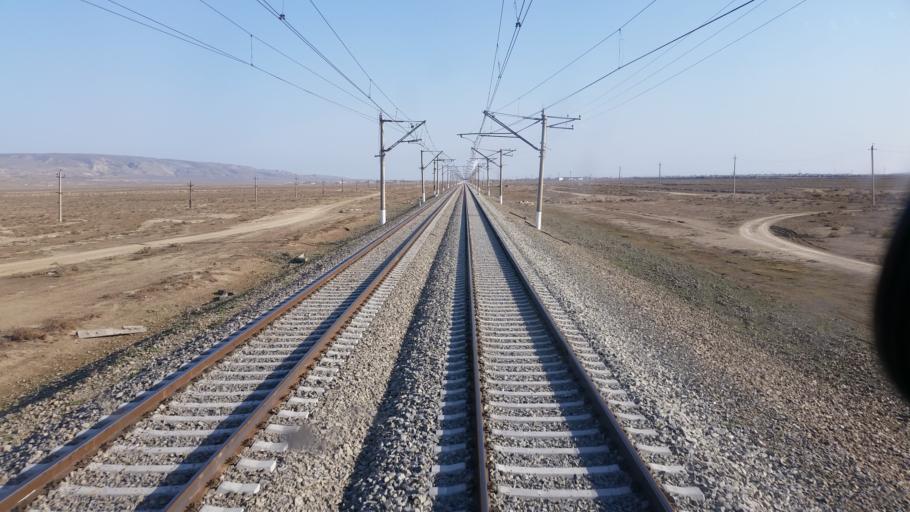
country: AZ
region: Baki
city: Qobustan
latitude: 39.9876
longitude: 49.2289
